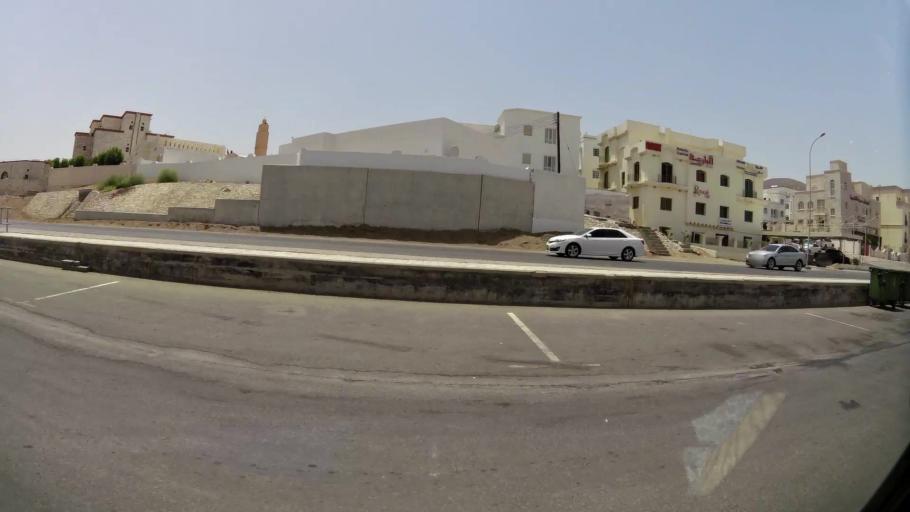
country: OM
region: Muhafazat Masqat
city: Bawshar
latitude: 23.5871
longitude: 58.4400
